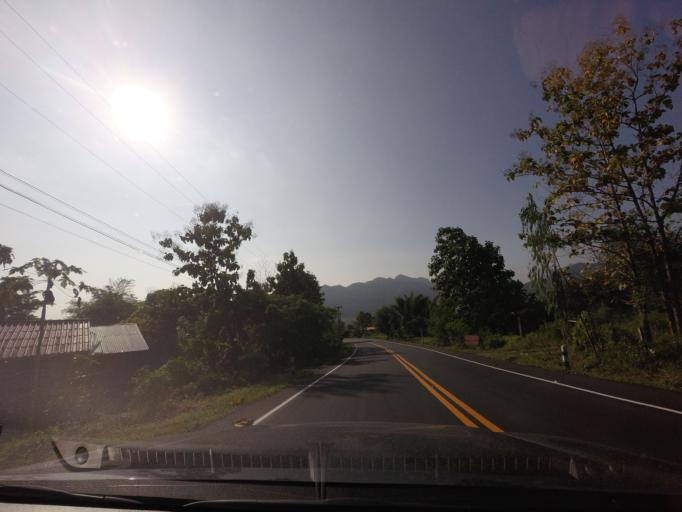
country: TH
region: Phetchabun
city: Lom Kao
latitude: 16.8751
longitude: 101.1303
